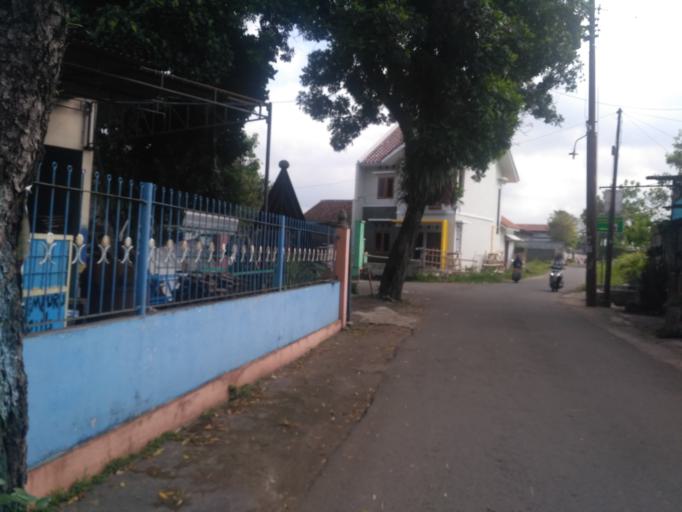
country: ID
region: Daerah Istimewa Yogyakarta
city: Yogyakarta
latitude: -7.7643
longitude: 110.3587
